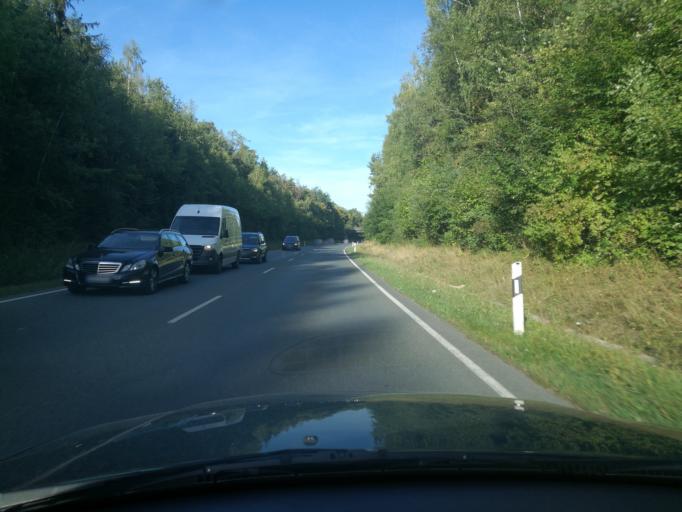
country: DE
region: Bavaria
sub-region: Regierungsbezirk Mittelfranken
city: Obermichelbach
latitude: 49.5693
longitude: 10.9475
